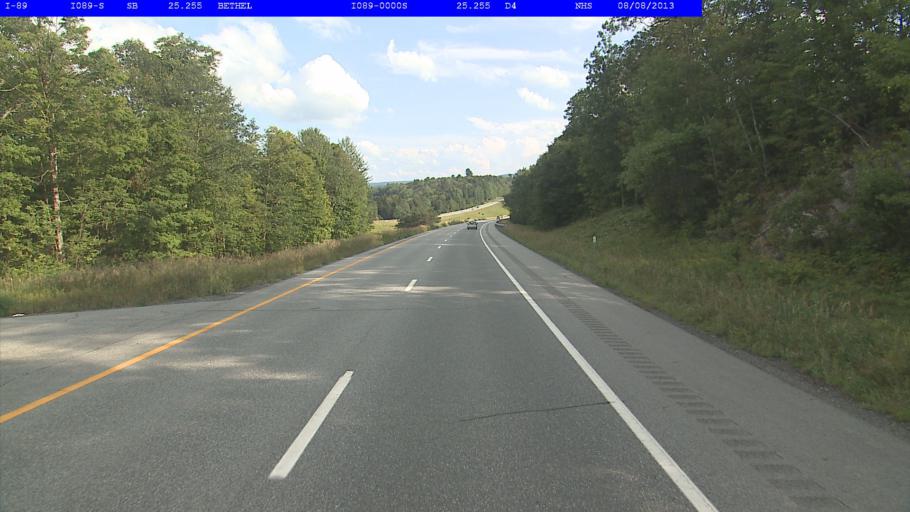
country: US
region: Vermont
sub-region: Orange County
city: Randolph
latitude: 43.8657
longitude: -72.6092
